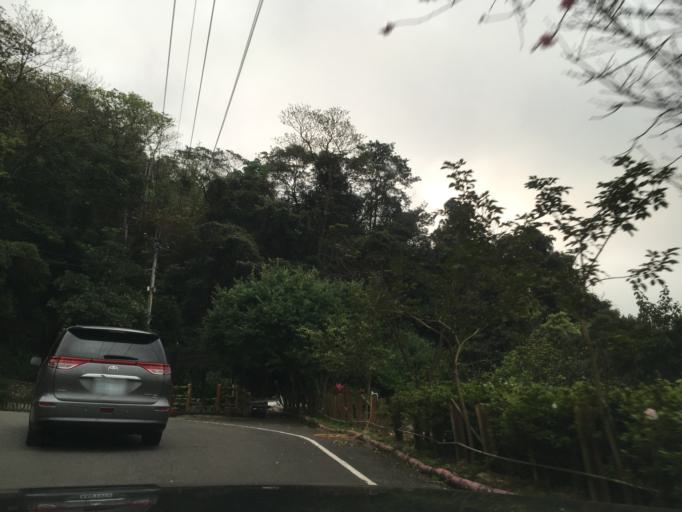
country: TW
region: Taiwan
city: Daxi
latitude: 24.8960
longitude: 121.3802
